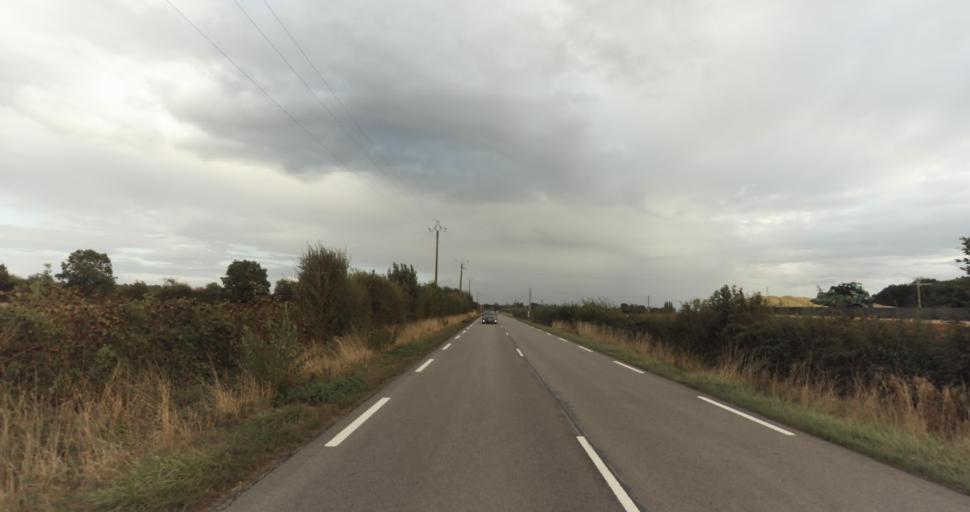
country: FR
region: Lower Normandy
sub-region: Departement de l'Orne
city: Vimoutiers
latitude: 48.9114
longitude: 0.2457
